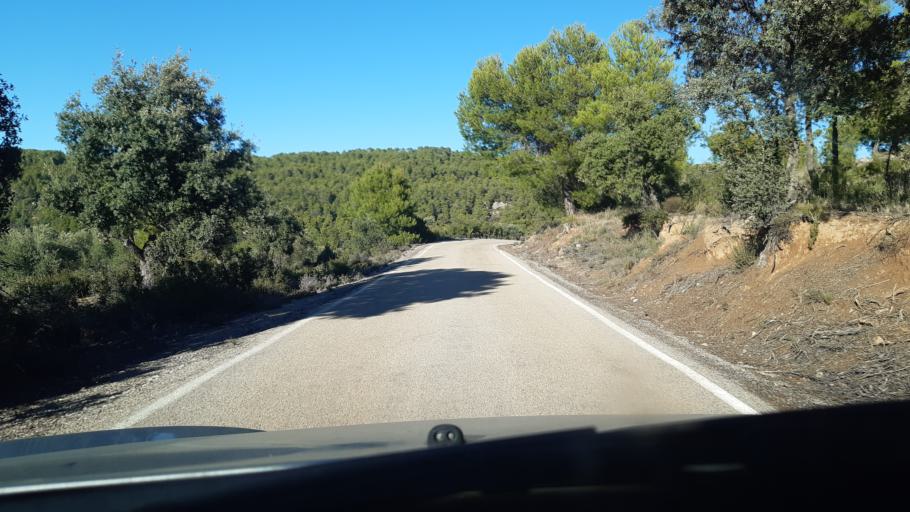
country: ES
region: Aragon
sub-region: Provincia de Teruel
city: Fornoles
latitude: 40.9034
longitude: -0.0083
